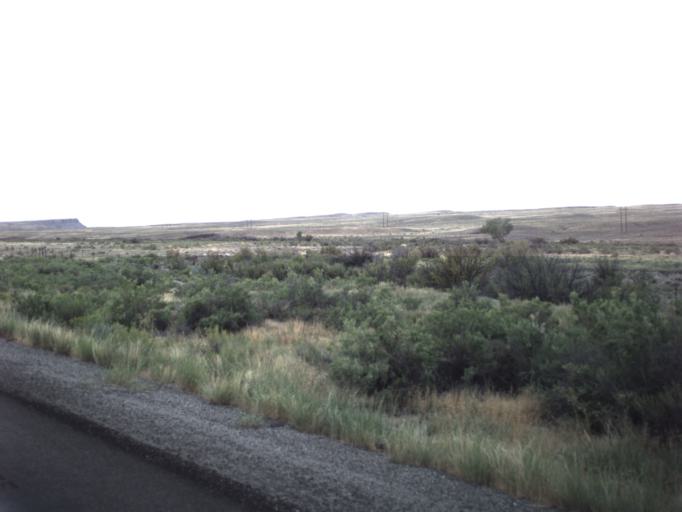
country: US
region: Utah
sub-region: Carbon County
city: East Carbon City
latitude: 39.4663
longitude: -110.4936
